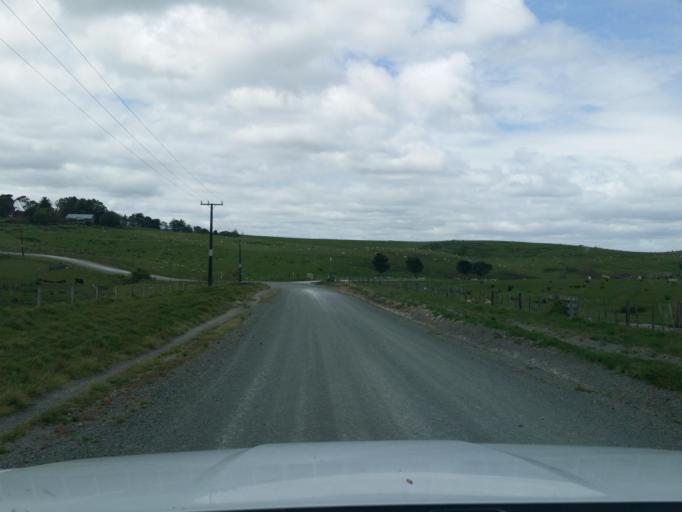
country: NZ
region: Auckland
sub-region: Auckland
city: Wellsford
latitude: -36.2884
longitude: 174.3309
